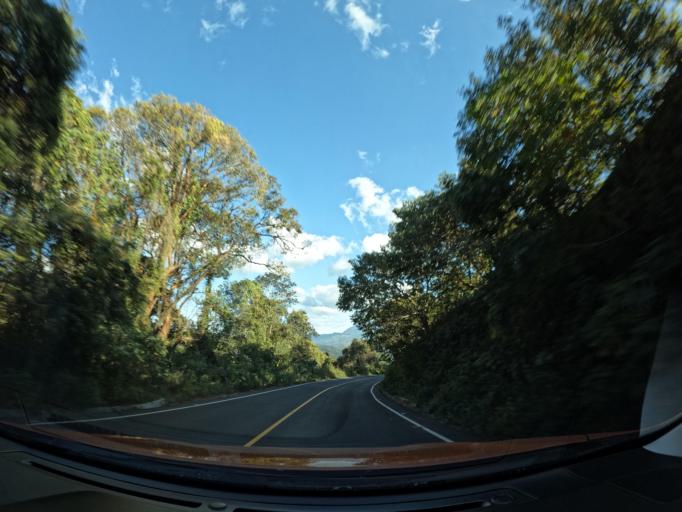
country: GT
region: Escuintla
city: Palin
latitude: 14.4540
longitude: -90.6947
